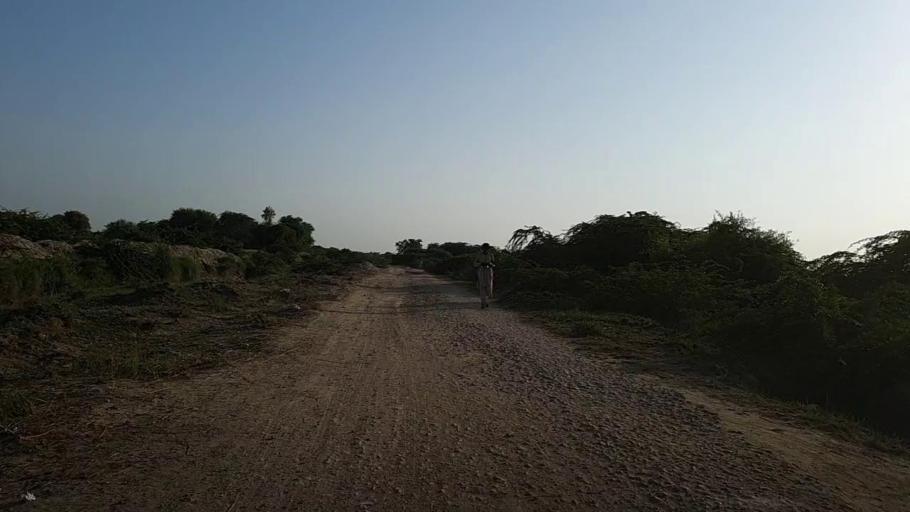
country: PK
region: Sindh
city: Kario
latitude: 24.7267
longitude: 68.6681
